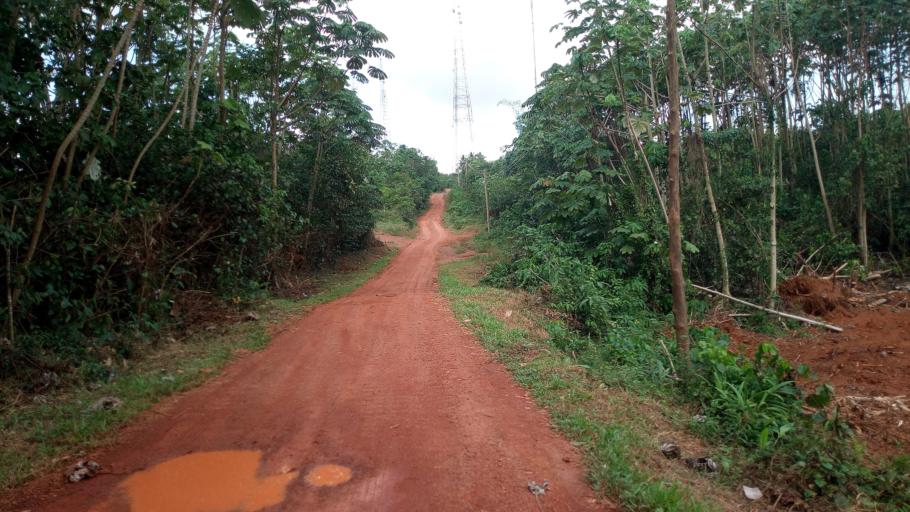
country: GH
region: Western
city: Tarkwa
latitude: 5.3011
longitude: -2.0044
